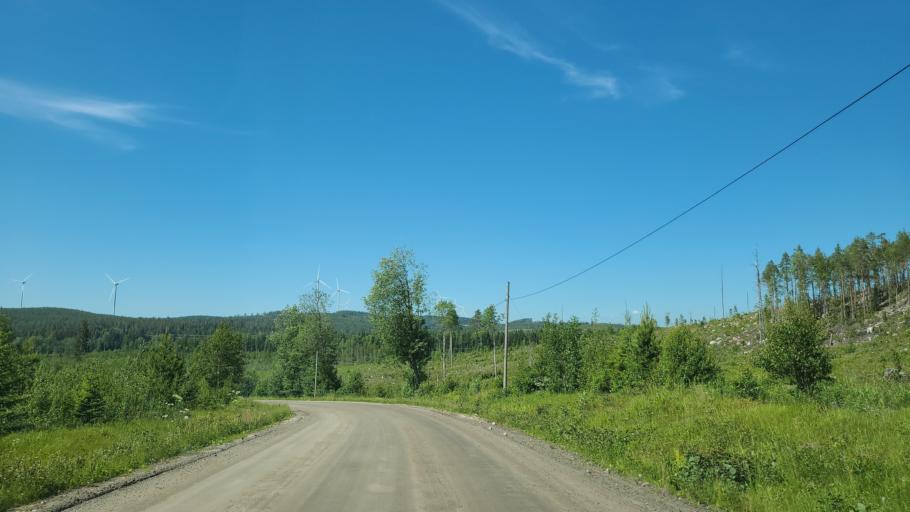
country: SE
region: Vaesterbotten
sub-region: Bjurholms Kommun
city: Bjurholm
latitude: 63.7050
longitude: 18.9105
